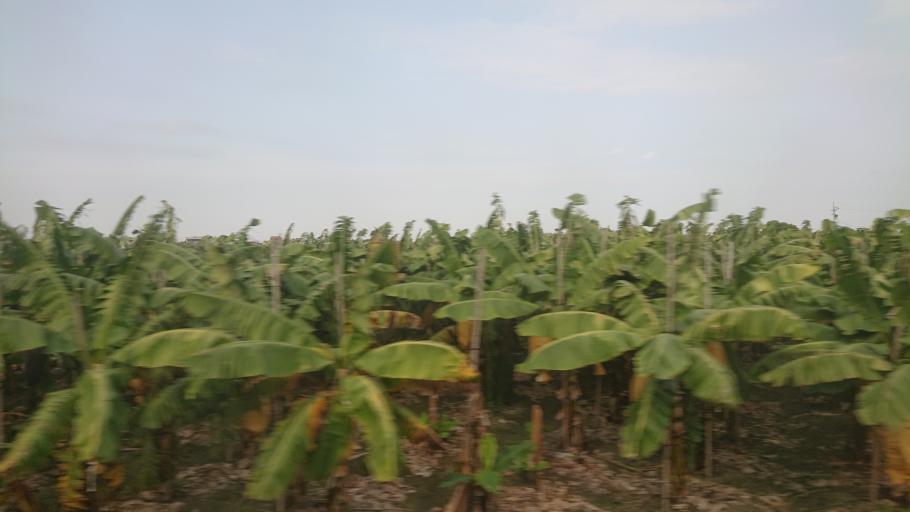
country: TW
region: Taiwan
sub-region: Yunlin
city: Douliu
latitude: 23.7409
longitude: 120.5890
